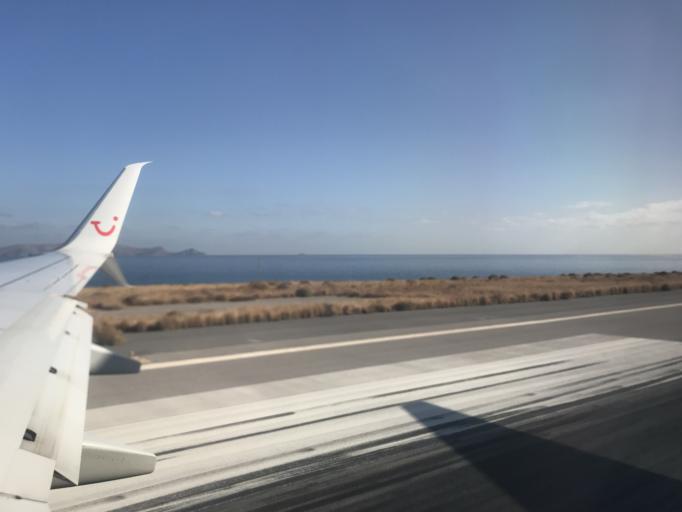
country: GR
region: Crete
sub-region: Nomos Irakleiou
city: Nea Alikarnassos
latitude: 35.3390
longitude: 25.1865
